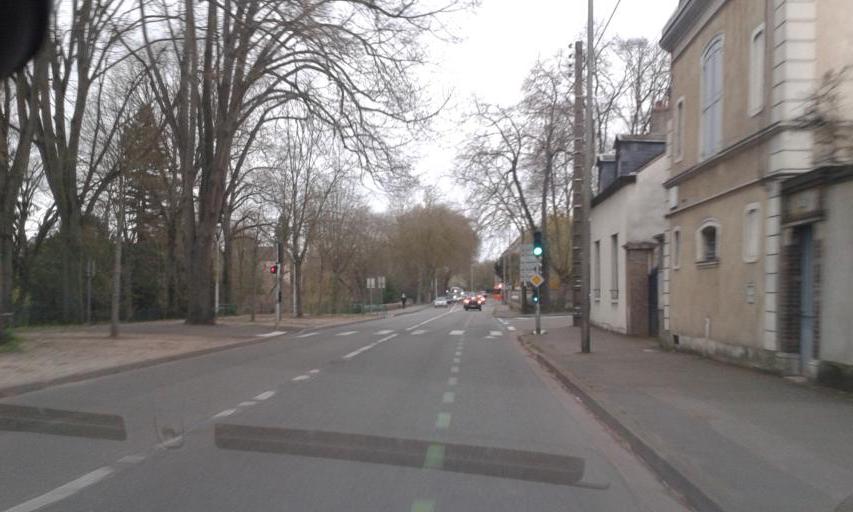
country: FR
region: Centre
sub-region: Departement d'Eure-et-Loir
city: Chartres
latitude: 48.4503
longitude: 1.4918
